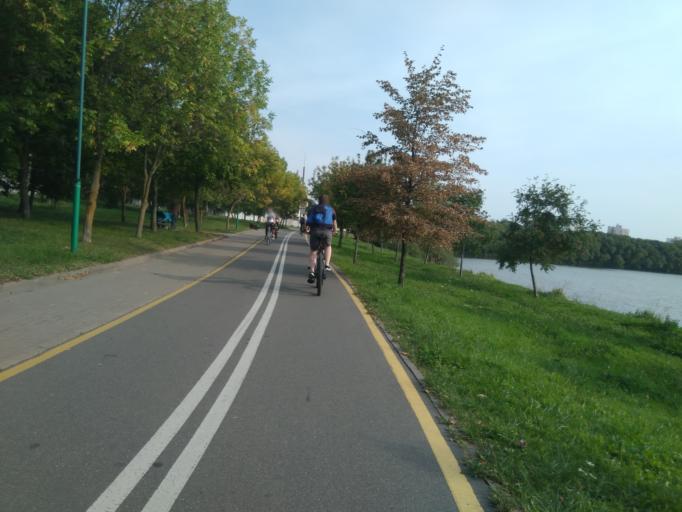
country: BY
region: Minsk
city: Minsk
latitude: 53.8828
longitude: 27.5736
